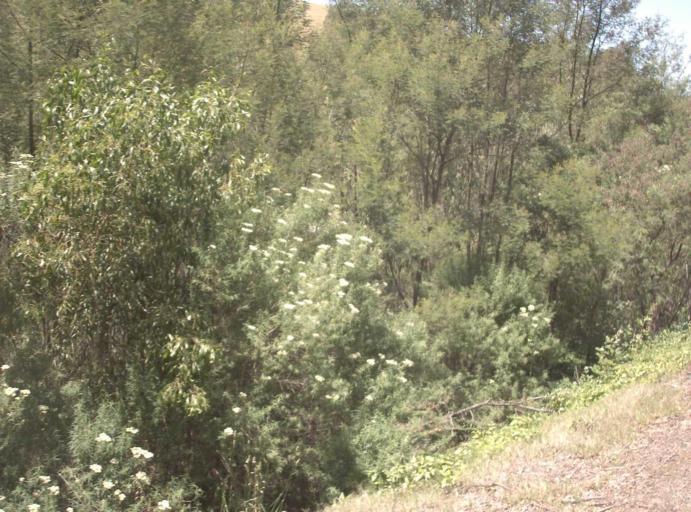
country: AU
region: Victoria
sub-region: East Gippsland
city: Bairnsdale
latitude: -37.4920
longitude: 147.8337
